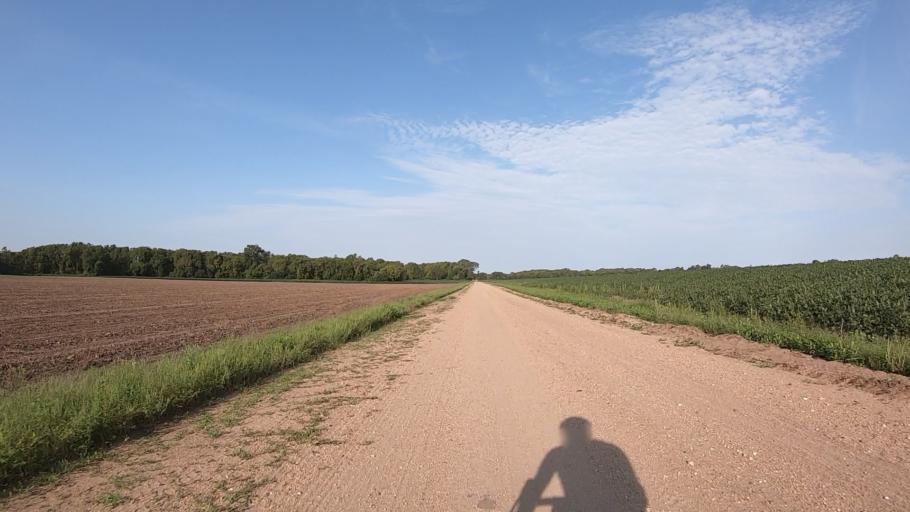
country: US
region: Kansas
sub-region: Marshall County
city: Blue Rapids
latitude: 39.6570
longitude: -96.8746
